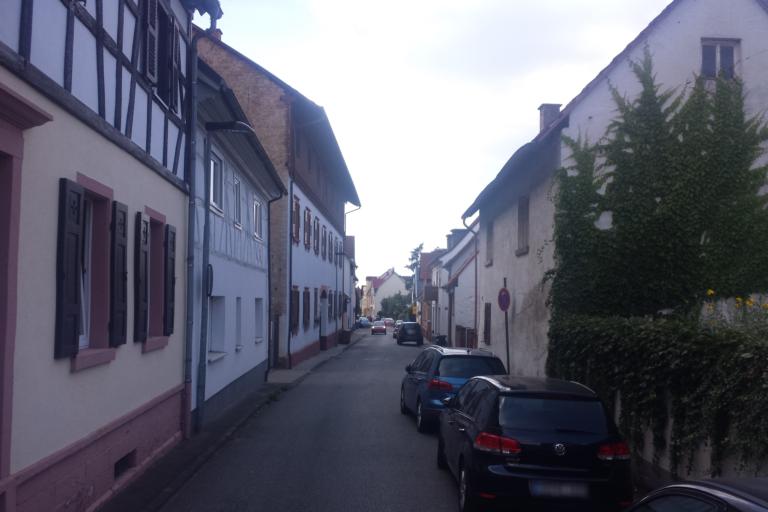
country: DE
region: Baden-Wuerttemberg
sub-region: Karlsruhe Region
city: Hemsbach
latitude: 49.5899
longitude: 8.6554
